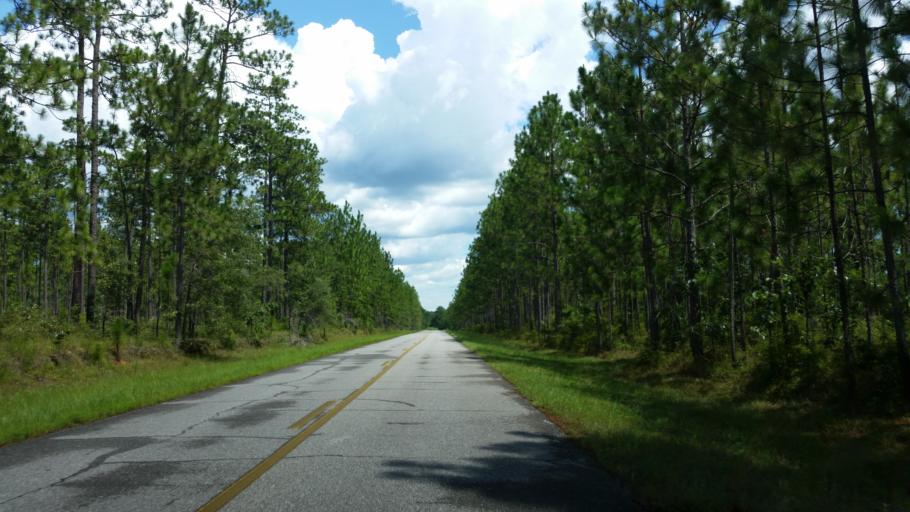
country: US
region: Florida
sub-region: Santa Rosa County
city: East Milton
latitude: 30.7396
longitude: -86.8220
